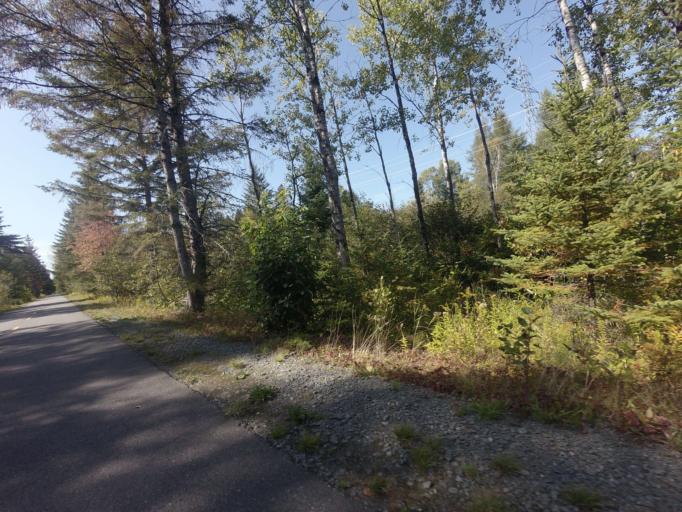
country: CA
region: Quebec
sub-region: Laurentides
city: Mont-Tremblant
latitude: 46.1286
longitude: -74.5593
